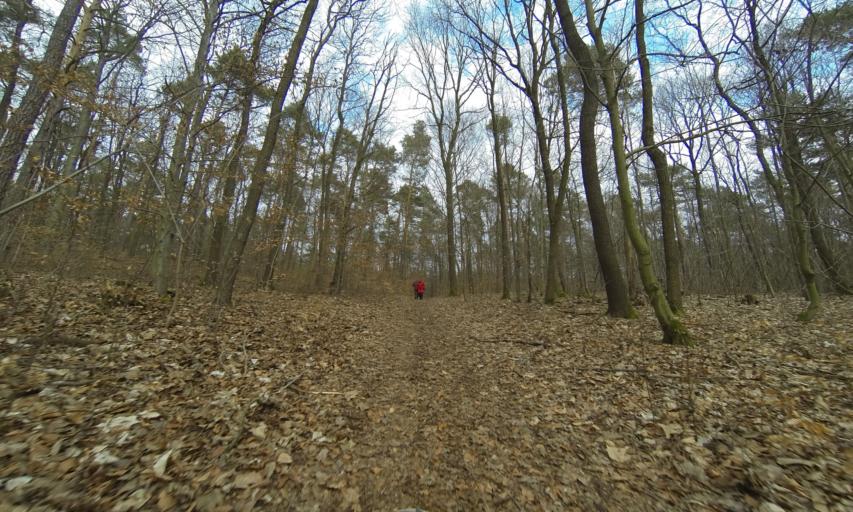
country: DE
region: Saxony
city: Radebeul
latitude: 51.1095
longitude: 13.7104
